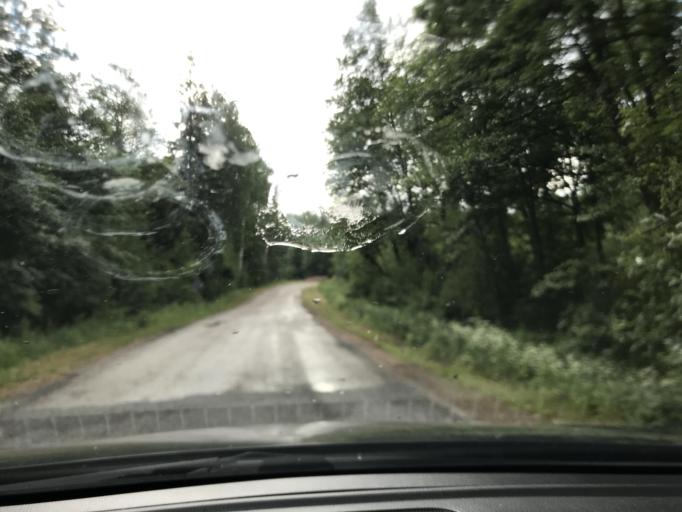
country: LV
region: Alsunga
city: Alsunga
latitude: 56.9836
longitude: 21.6311
